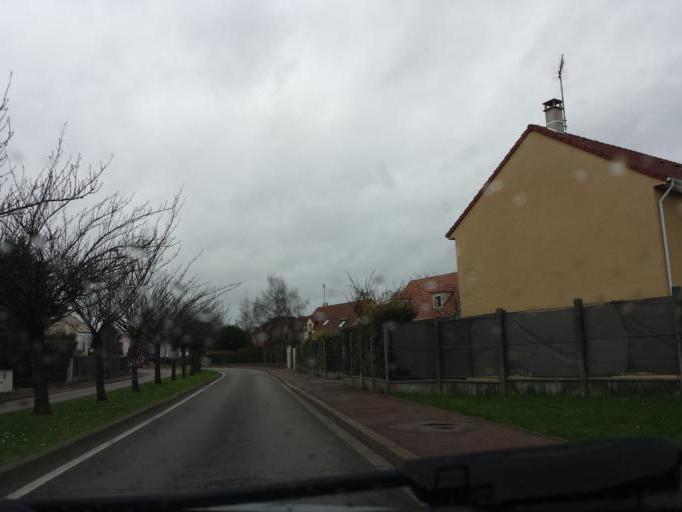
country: FR
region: Ile-de-France
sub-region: Departement du Val-d'Oise
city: Franconville
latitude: 48.9893
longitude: 2.2295
